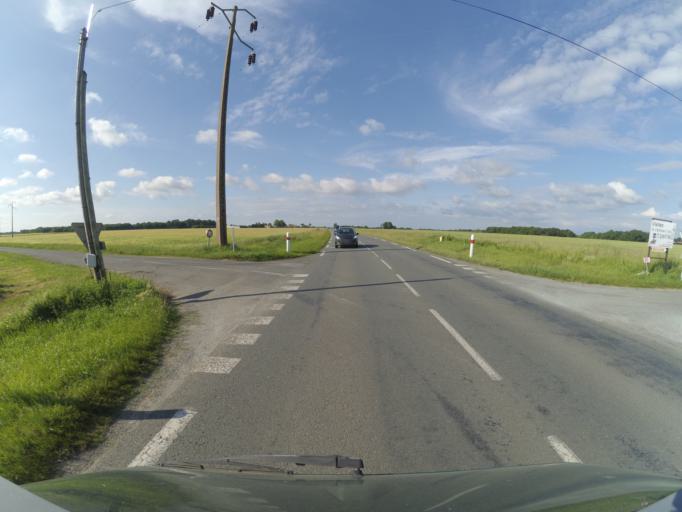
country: FR
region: Poitou-Charentes
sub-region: Departement de la Charente-Maritime
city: Le Gua
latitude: 45.7391
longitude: -0.9506
